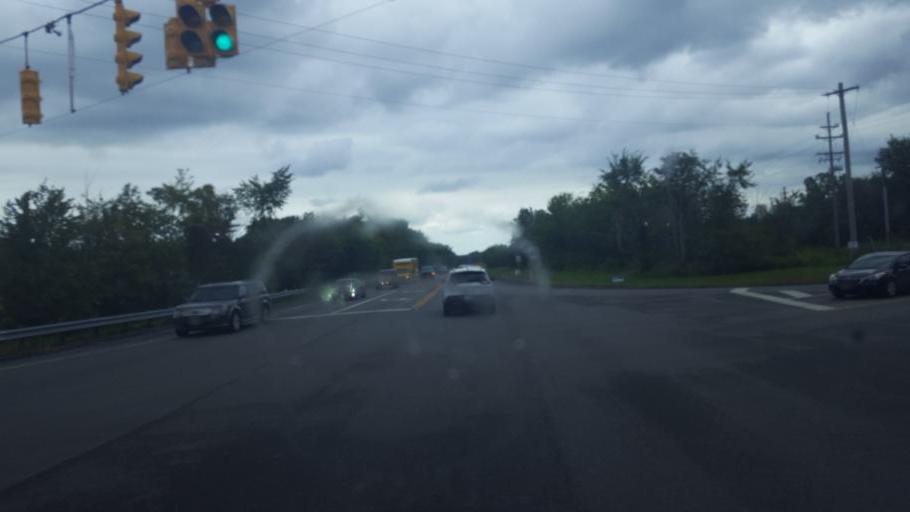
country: US
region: Ohio
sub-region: Lake County
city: Painesville
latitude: 41.6471
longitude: -81.2417
